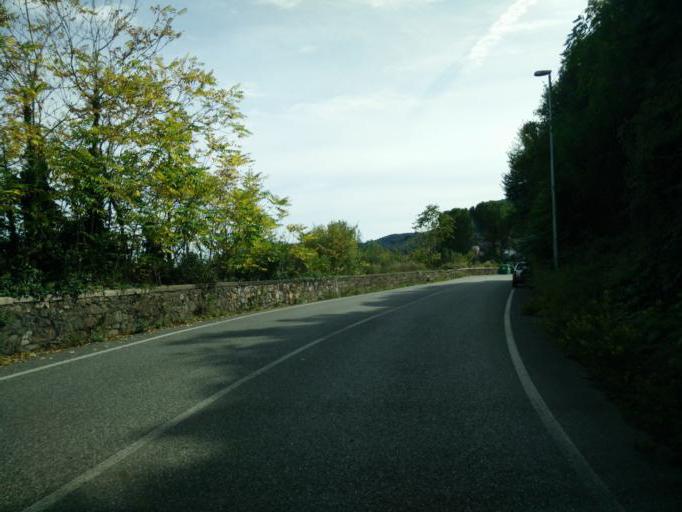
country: IT
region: Liguria
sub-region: Provincia di La Spezia
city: Le Grazie
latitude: 44.0861
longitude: 9.8216
